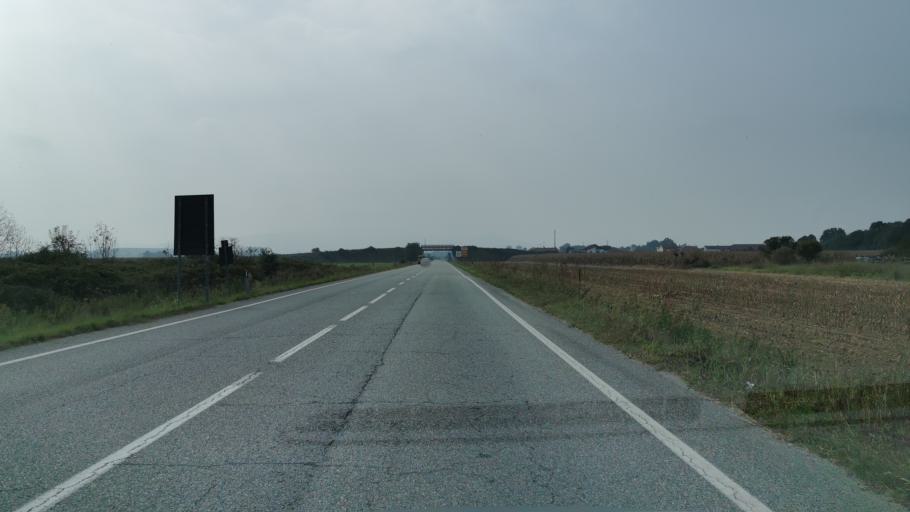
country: IT
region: Piedmont
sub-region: Provincia di Torino
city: Montanaro
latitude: 45.2374
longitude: 7.8647
